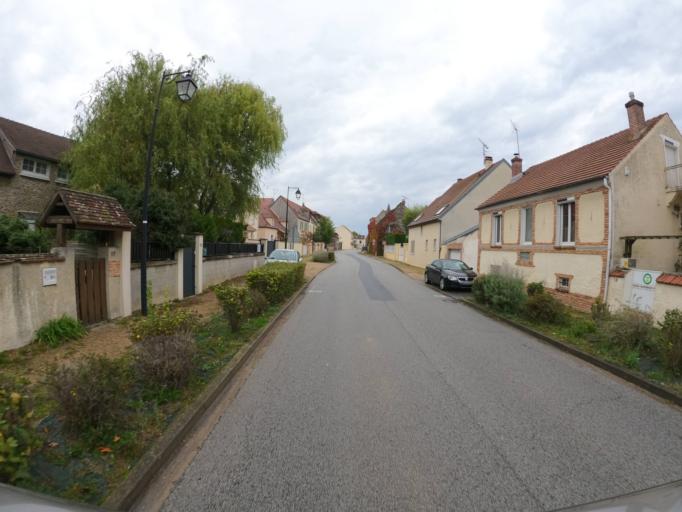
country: FR
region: Ile-de-France
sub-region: Departement de Seine-et-Marne
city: Serris
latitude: 48.8151
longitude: 2.7914
